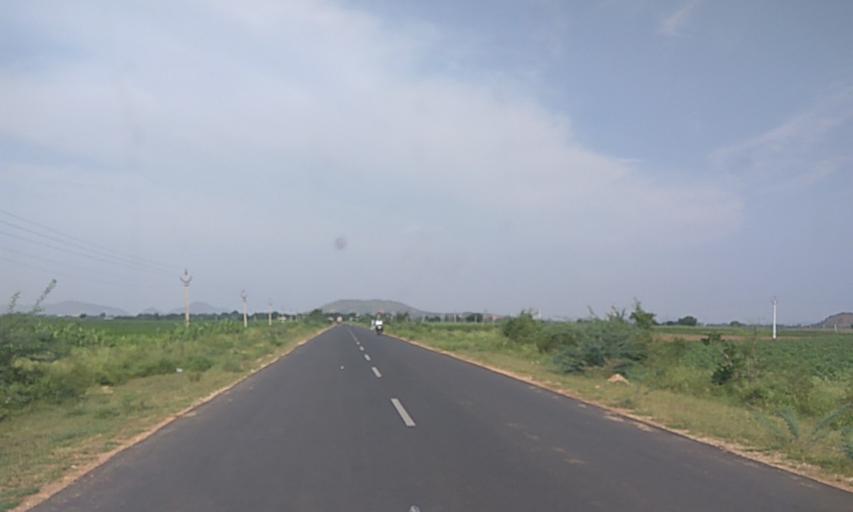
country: IN
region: Andhra Pradesh
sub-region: Prakasam
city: Markapur
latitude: 15.7565
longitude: 79.2317
